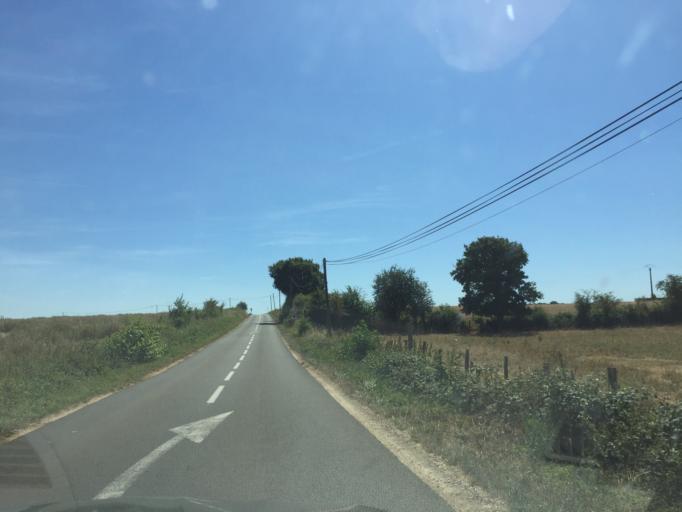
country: FR
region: Poitou-Charentes
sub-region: Departement de la Vienne
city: Vivonne
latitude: 46.4375
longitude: 0.3100
